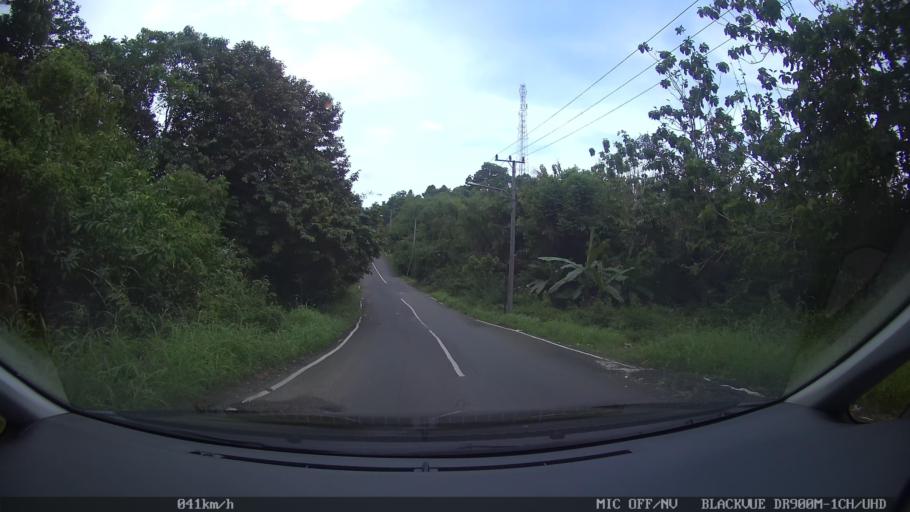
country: ID
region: Lampung
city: Bandarlampung
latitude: -5.4278
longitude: 105.1988
